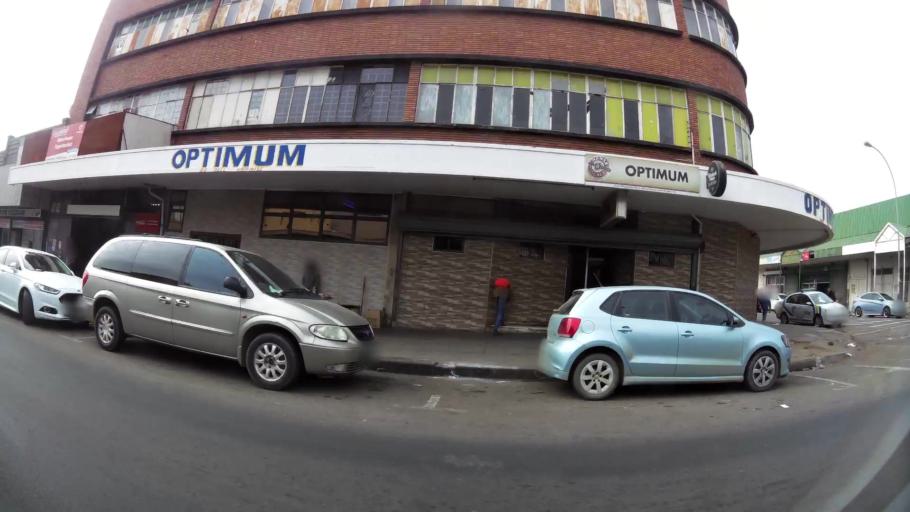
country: ZA
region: Orange Free State
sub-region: Mangaung Metropolitan Municipality
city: Bloemfontein
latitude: -29.1225
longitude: 26.2248
